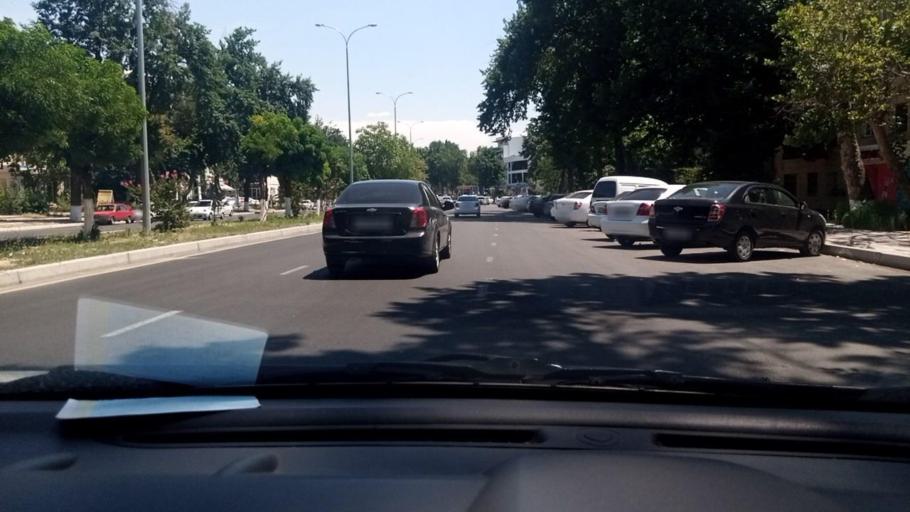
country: UZ
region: Toshkent Shahri
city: Tashkent
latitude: 41.2900
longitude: 69.2008
